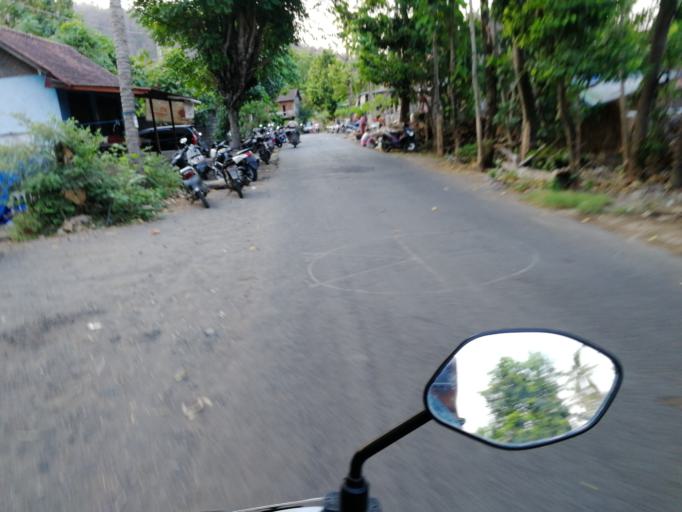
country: ID
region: Bali
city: Biaslantang Kaler
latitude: -8.3558
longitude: 115.6892
